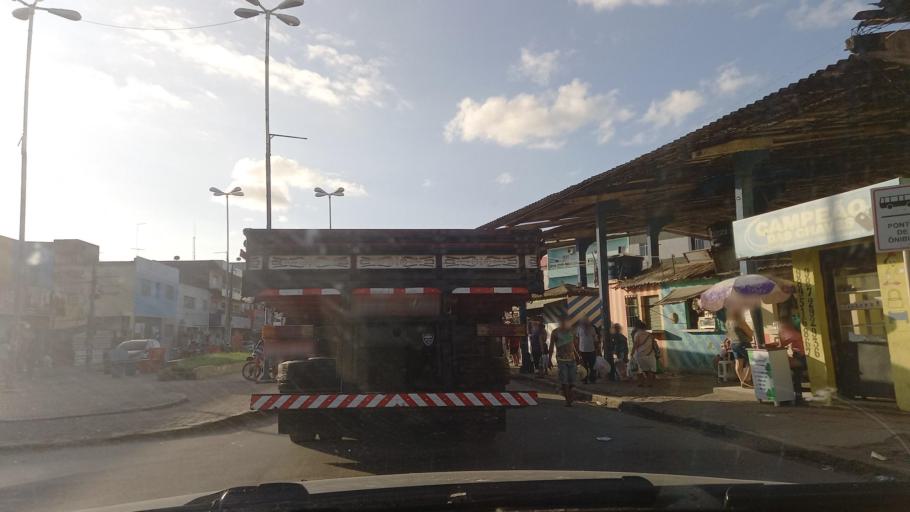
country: BR
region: Pernambuco
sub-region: Vitoria De Santo Antao
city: Vitoria de Santo Antao
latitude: -8.1212
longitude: -35.2949
